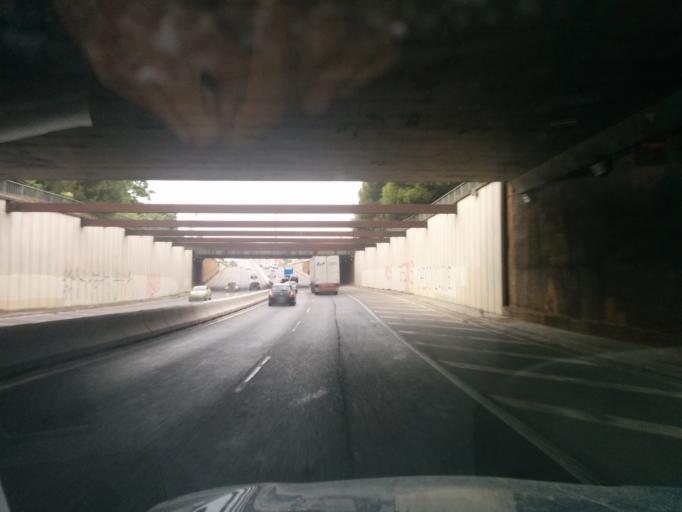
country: ES
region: Andalusia
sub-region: Provincia de Sevilla
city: Sevilla
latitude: 37.4161
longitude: -5.9735
